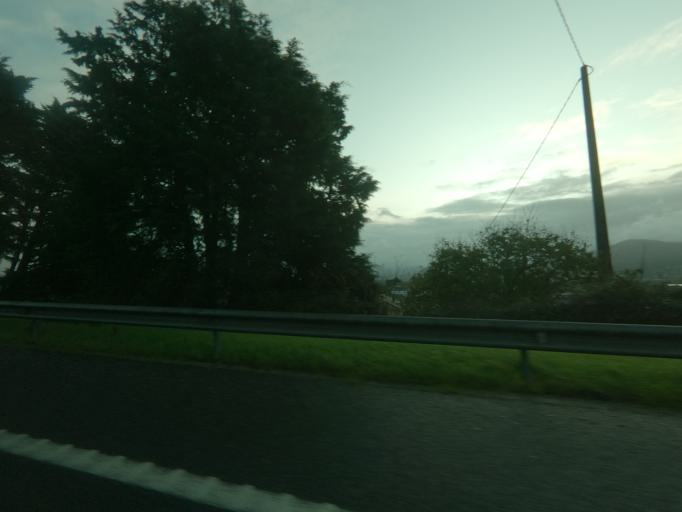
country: ES
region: Galicia
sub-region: Provincia de Pontevedra
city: Tui
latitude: 42.0605
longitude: -8.6499
